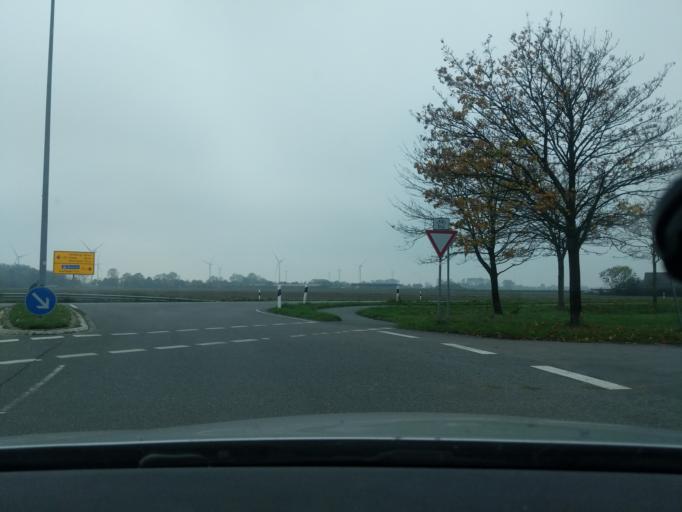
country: DE
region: Lower Saxony
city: Cuxhaven
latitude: 53.8266
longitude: 8.7627
